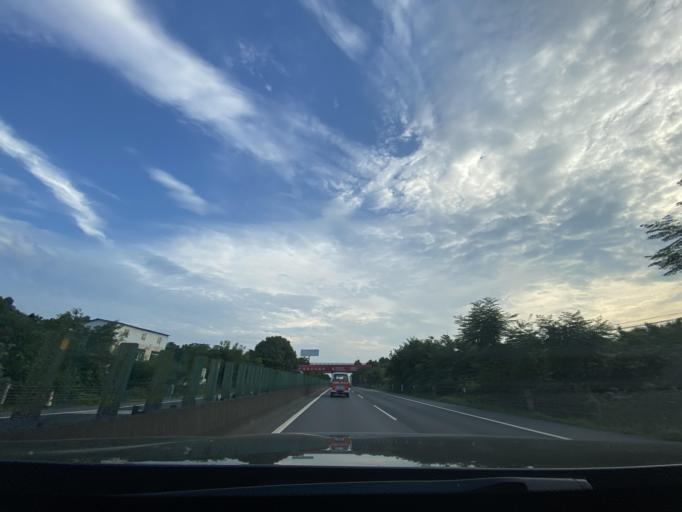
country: CN
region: Sichuan
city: Luojiang
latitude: 31.4075
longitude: 104.5758
